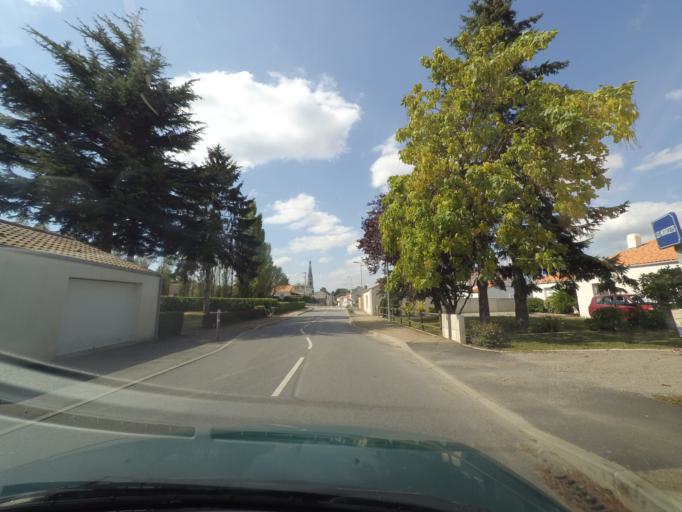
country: FR
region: Pays de la Loire
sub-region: Departement de la Loire-Atlantique
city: Saint-Hilaire-de-Chaleons
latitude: 47.1020
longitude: -1.8606
